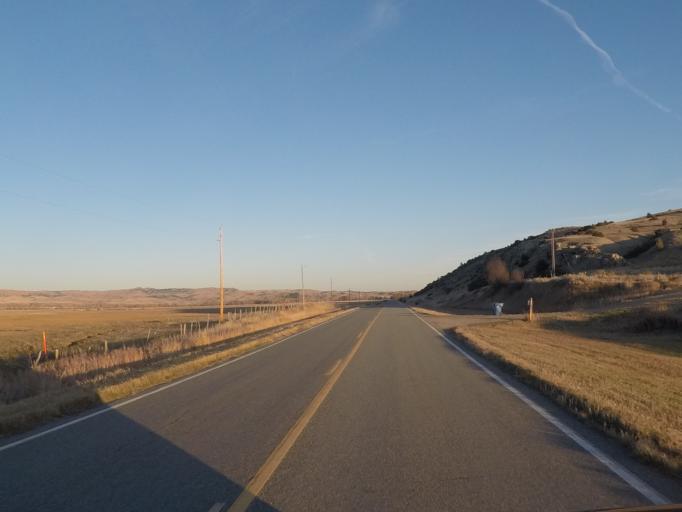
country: US
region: Montana
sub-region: Sweet Grass County
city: Big Timber
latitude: 45.7833
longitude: -109.8317
